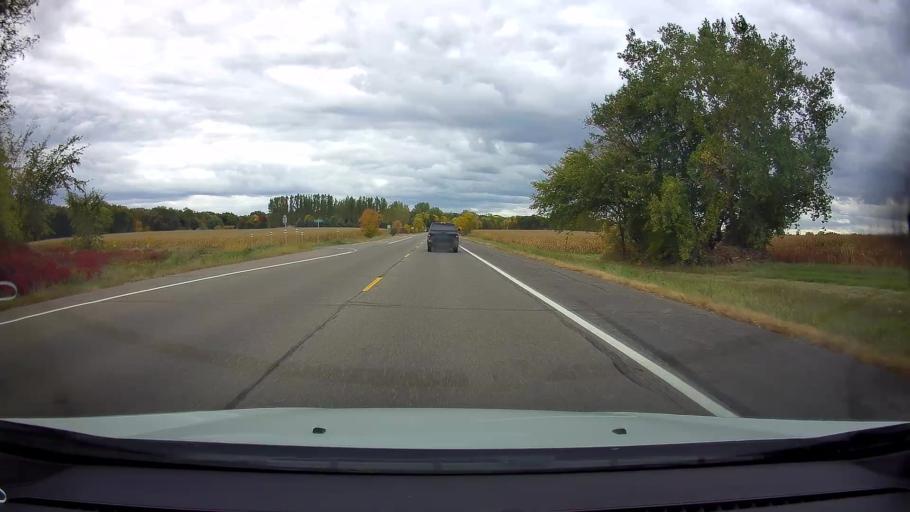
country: US
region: Minnesota
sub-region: Chisago County
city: Chisago City
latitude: 45.3484
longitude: -92.9118
